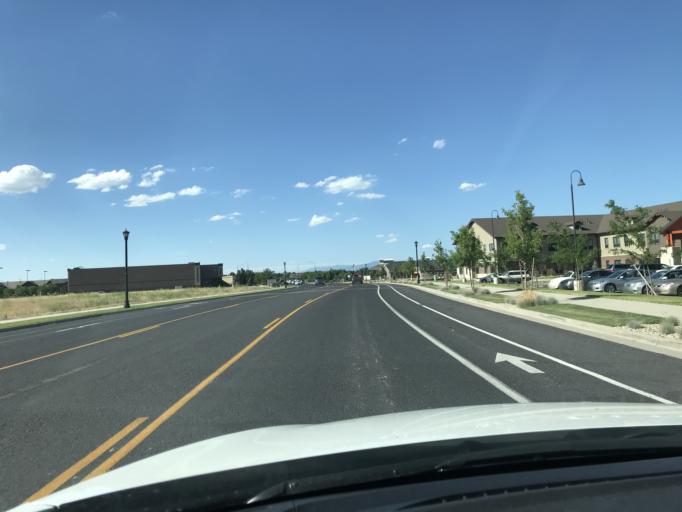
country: US
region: Utah
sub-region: Salt Lake County
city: South Jordan Heights
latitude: 40.5588
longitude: -111.9725
